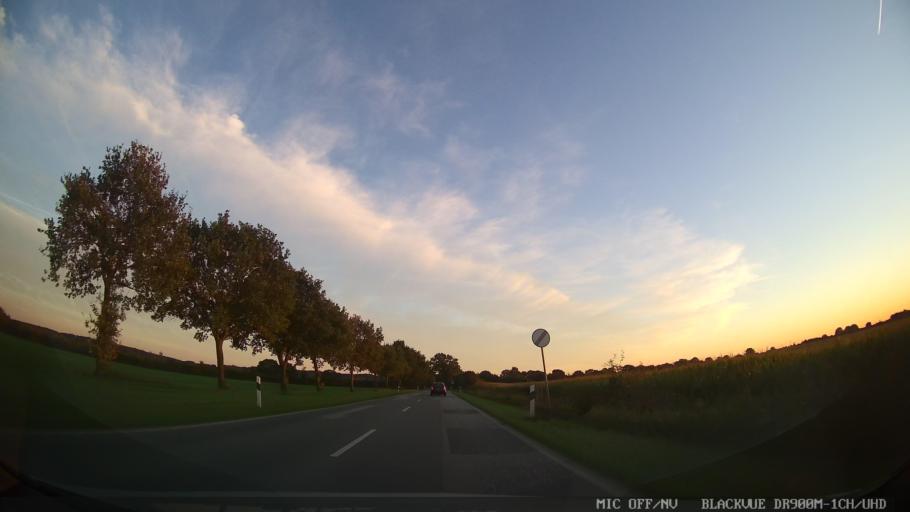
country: DE
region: Schleswig-Holstein
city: Susel
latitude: 54.0404
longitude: 10.6804
